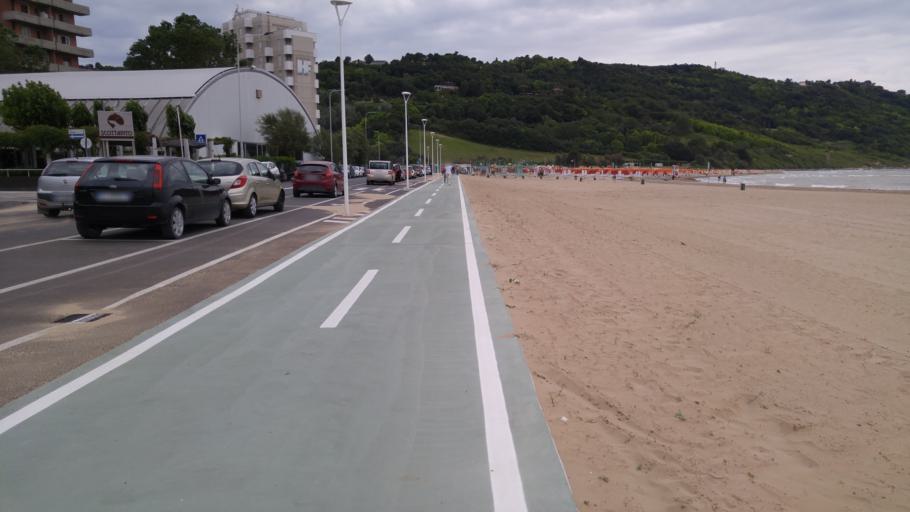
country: IT
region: The Marches
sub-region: Provincia di Pesaro e Urbino
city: Pesaro
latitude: 43.9225
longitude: 12.9009
